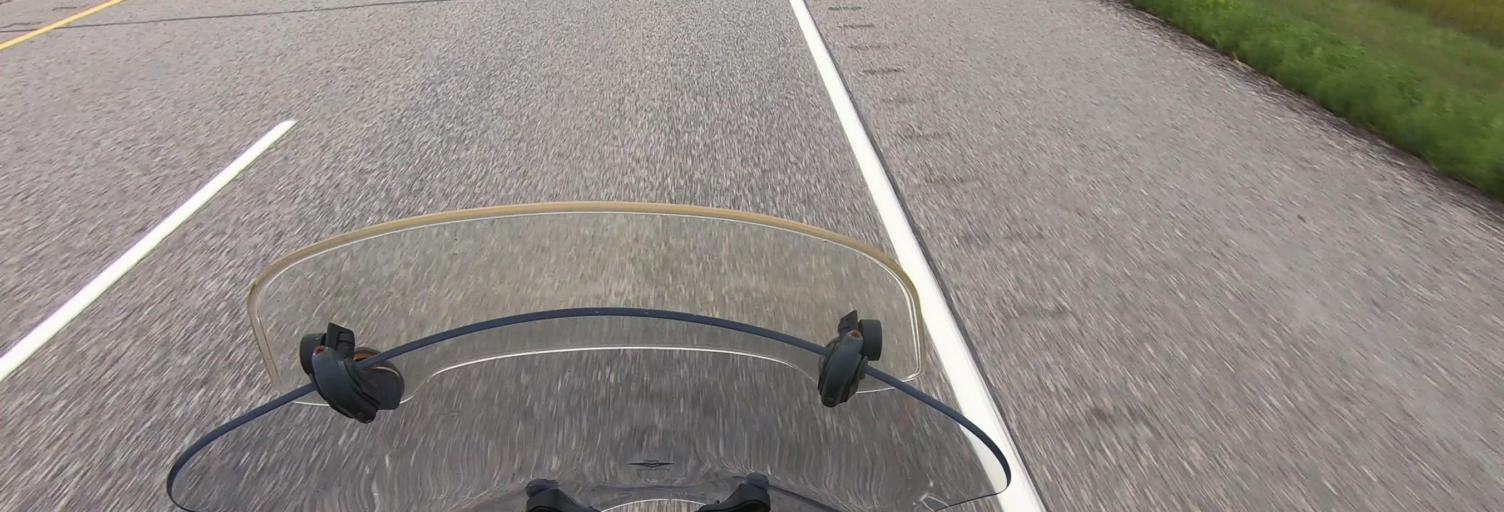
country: CA
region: Manitoba
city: Portage la Prairie
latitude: 49.9752
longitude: -98.6454
